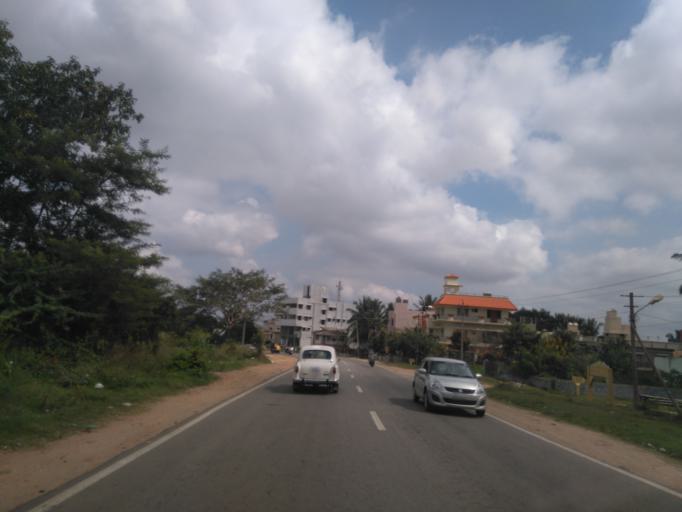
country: IN
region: Karnataka
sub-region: Mysore
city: Mysore
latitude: 12.3002
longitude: 76.6936
